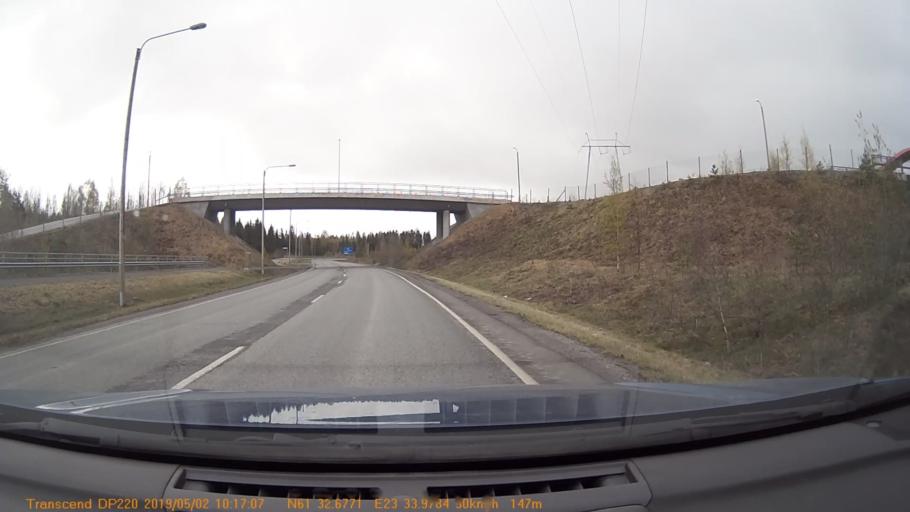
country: FI
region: Pirkanmaa
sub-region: Tampere
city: Yloejaervi
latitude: 61.5446
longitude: 23.5663
